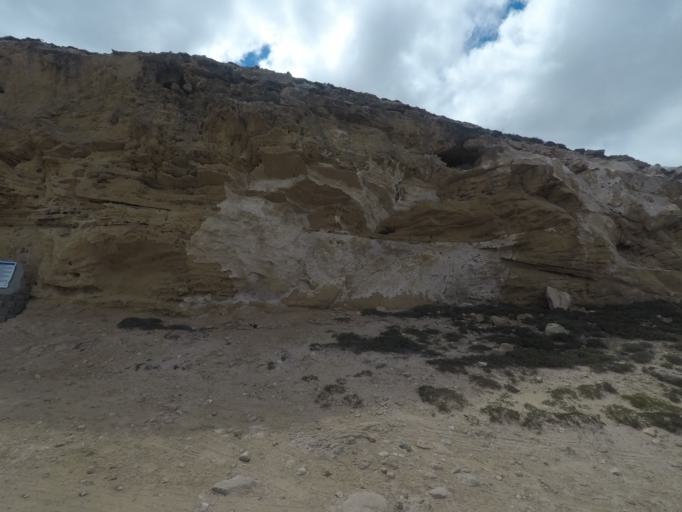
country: PT
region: Madeira
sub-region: Porto Santo
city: Vila de Porto Santo
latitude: 33.0676
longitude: -16.2969
